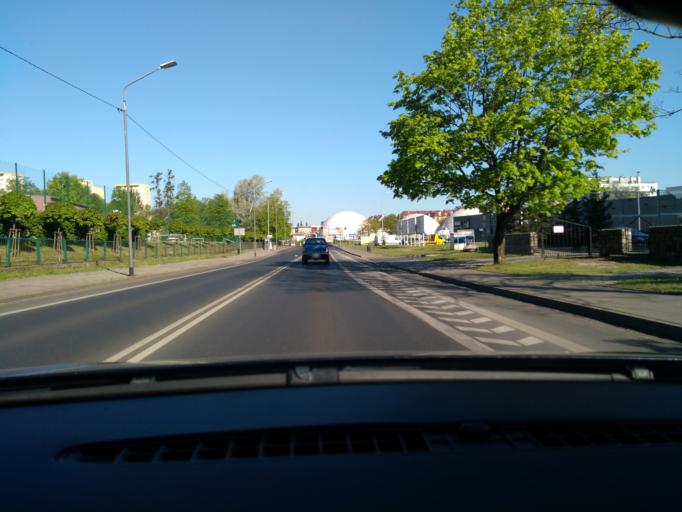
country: PL
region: West Pomeranian Voivodeship
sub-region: Szczecin
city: Szczecin
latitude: 53.4405
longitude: 14.5565
